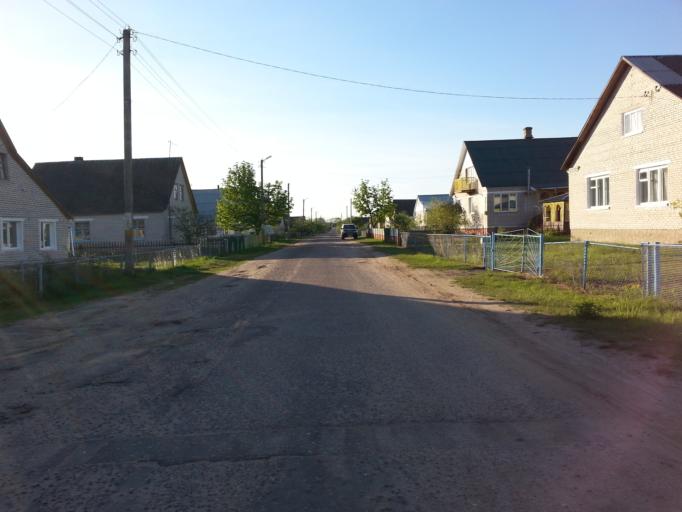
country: BY
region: Minsk
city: Narach
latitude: 54.9288
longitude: 26.6816
